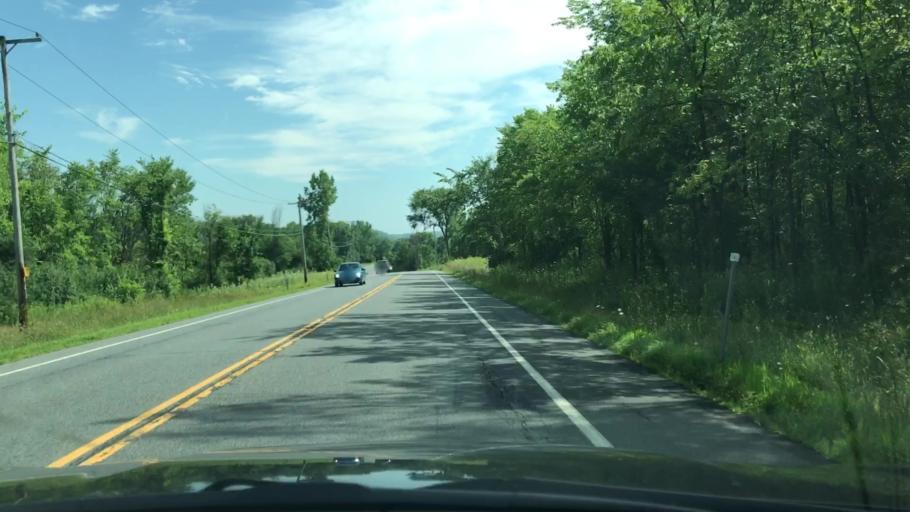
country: US
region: New York
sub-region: Washington County
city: Whitehall
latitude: 43.5225
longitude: -73.4139
